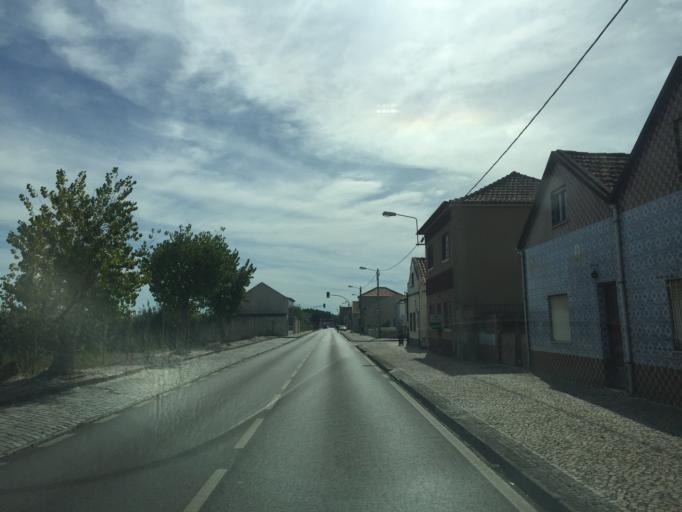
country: PT
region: Coimbra
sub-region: Figueira da Foz
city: Figueira da Foz
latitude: 40.1274
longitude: -8.8529
